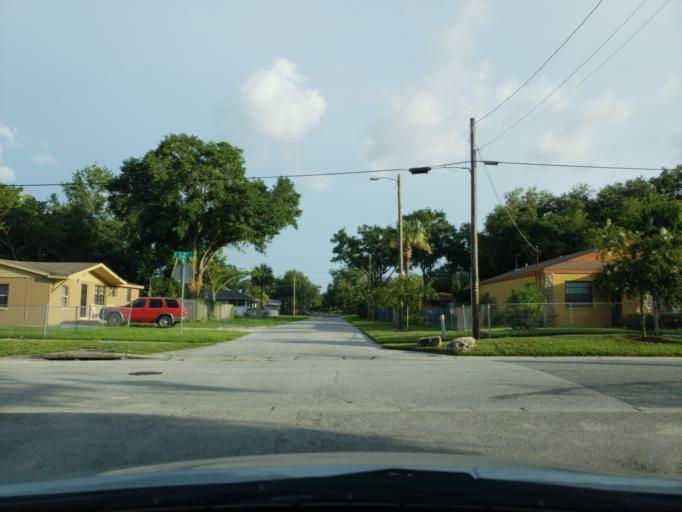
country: US
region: Florida
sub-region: Hillsborough County
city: Tampa
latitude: 27.9797
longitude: -82.4415
